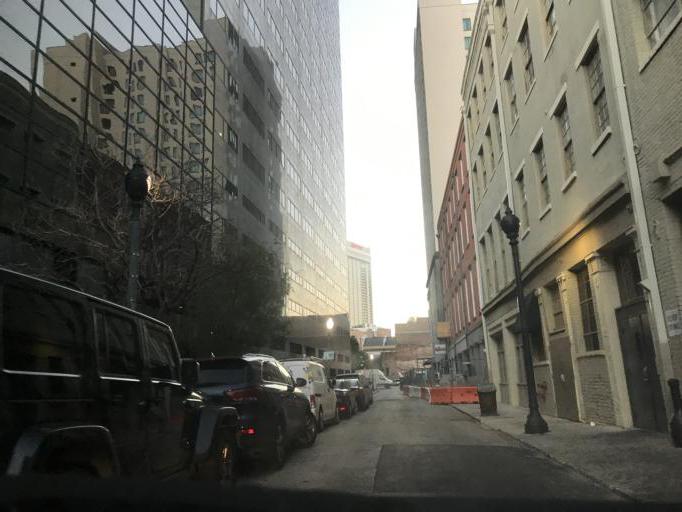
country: US
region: Louisiana
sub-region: Orleans Parish
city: New Orleans
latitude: 29.9479
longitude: -90.0678
